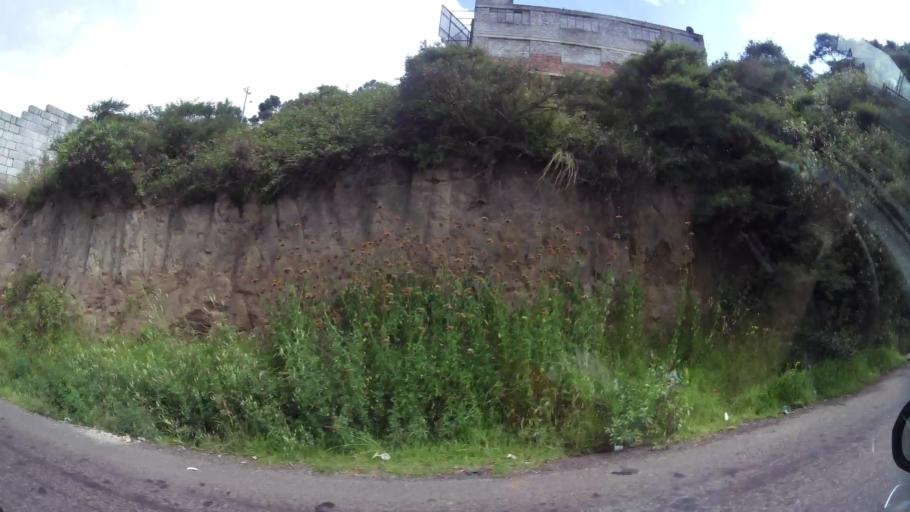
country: EC
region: Pichincha
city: Quito
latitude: -0.0962
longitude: -78.4655
